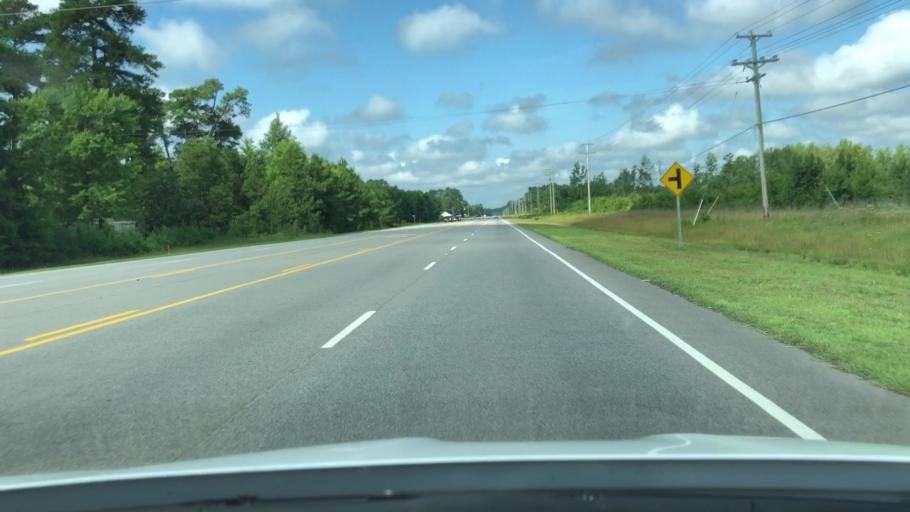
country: US
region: North Carolina
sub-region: Bertie County
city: Windsor
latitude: 36.0260
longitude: -76.8097
